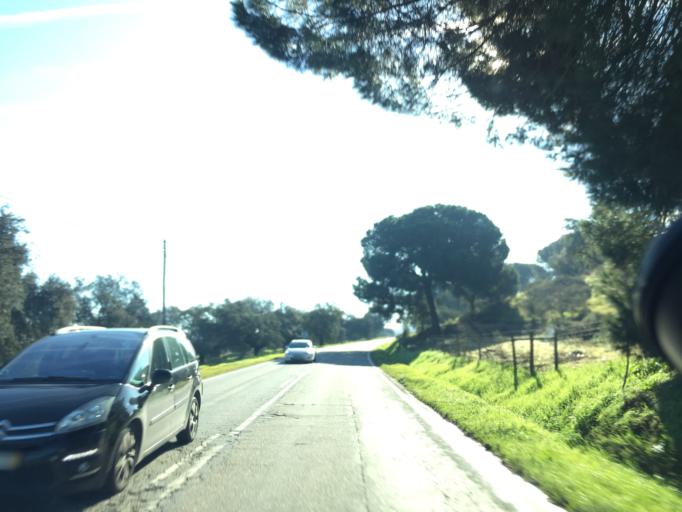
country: PT
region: Portalegre
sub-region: Ponte de Sor
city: Santo Andre
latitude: 38.9958
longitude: -8.3139
